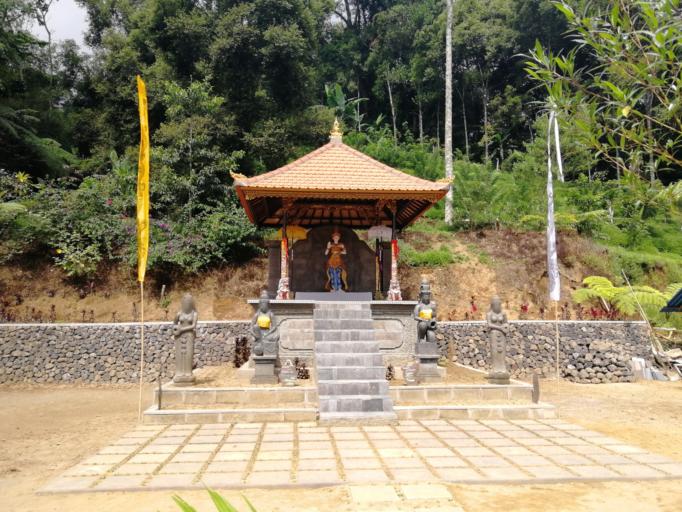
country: ID
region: Bali
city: Munduk
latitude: -8.3283
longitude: 115.0651
